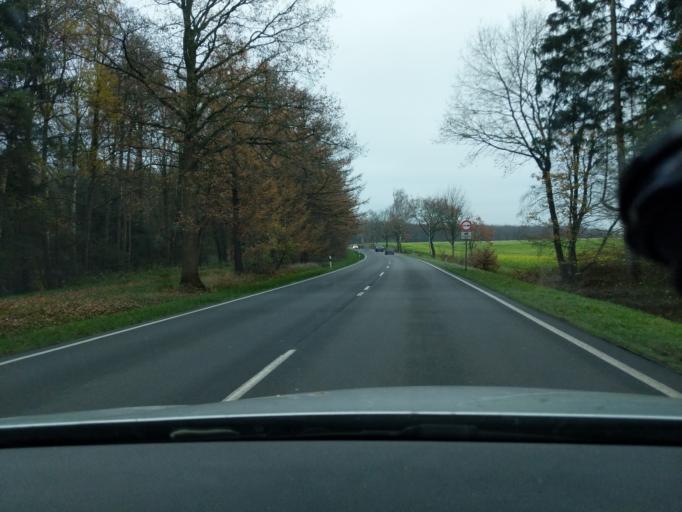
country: DE
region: Lower Saxony
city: Zeven
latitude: 53.2506
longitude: 9.2745
